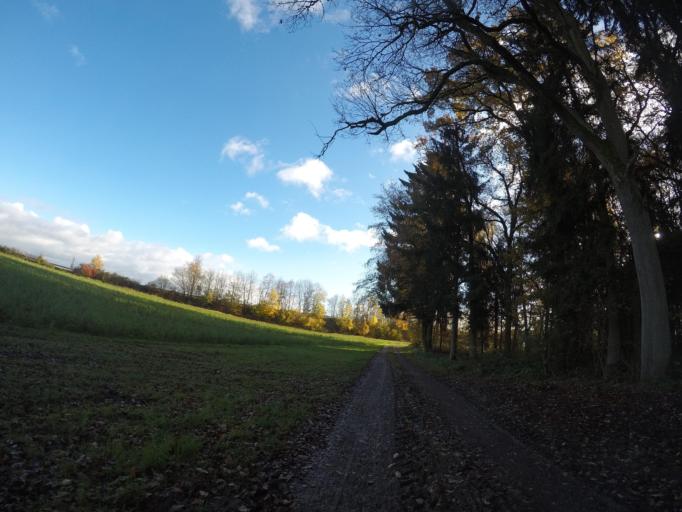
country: DE
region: Baden-Wuerttemberg
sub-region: Tuebingen Region
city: Bernstadt
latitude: 48.4549
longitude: 10.0238
